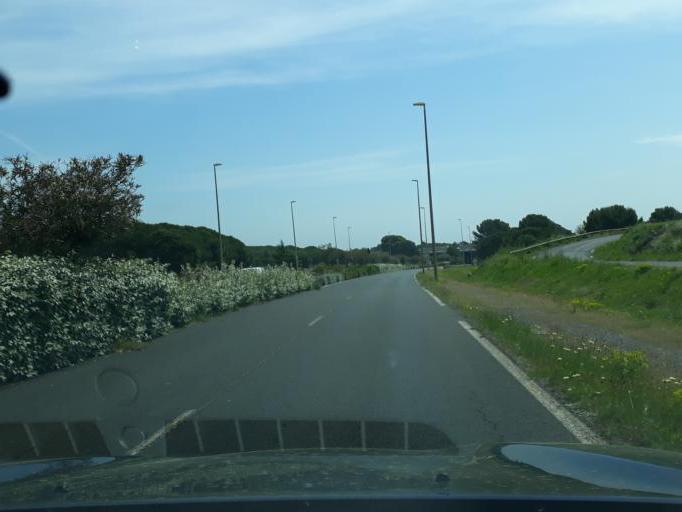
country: FR
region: Languedoc-Roussillon
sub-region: Departement de l'Herault
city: Le Cap d'Agde
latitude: 43.2949
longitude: 3.5000
